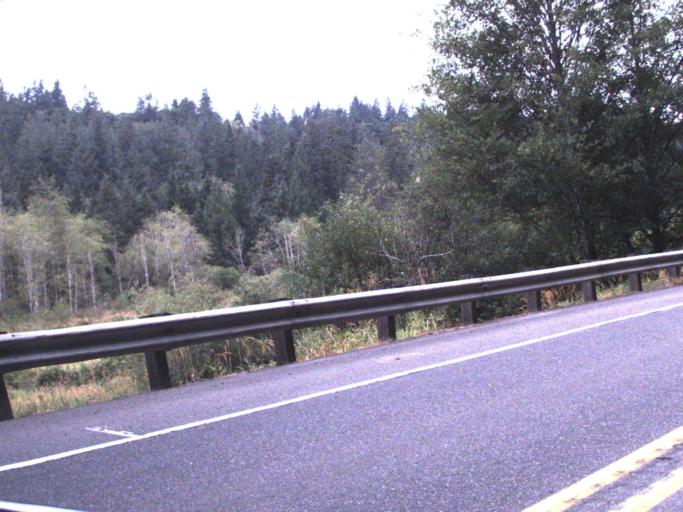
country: US
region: Washington
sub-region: King County
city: Ames Lake
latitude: 47.6284
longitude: -121.9942
